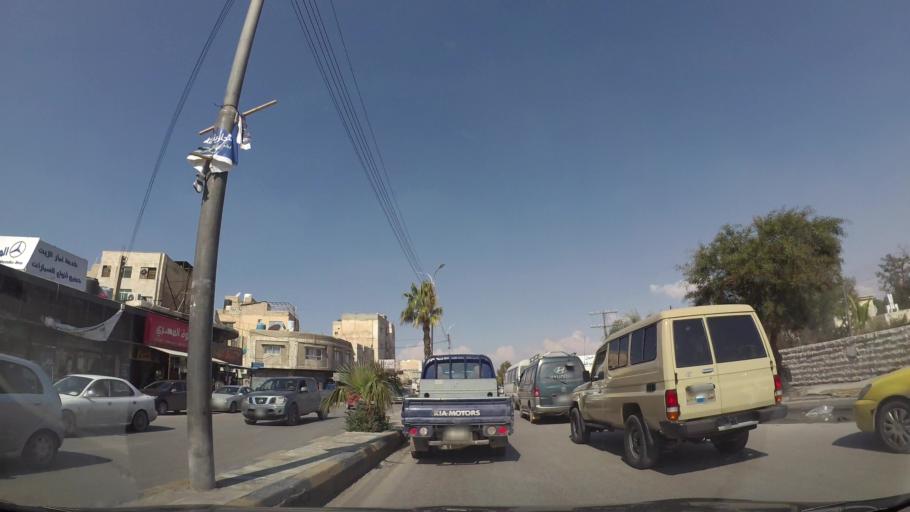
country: JO
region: Zarqa
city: Zarqa
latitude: 32.0660
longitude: 36.0956
